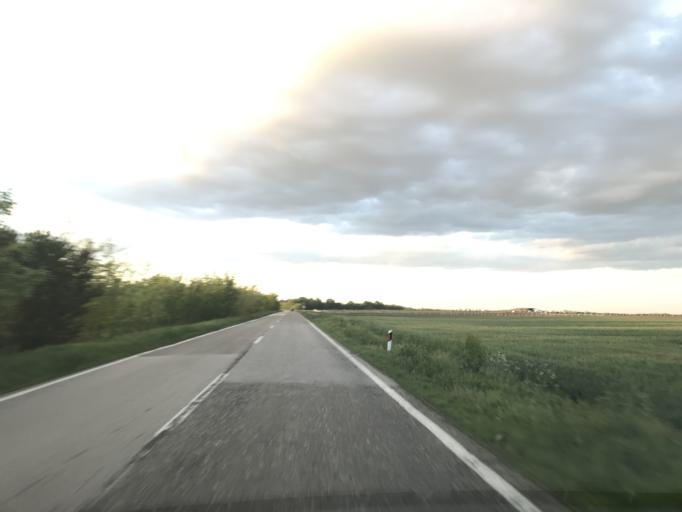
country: RS
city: Banatsko Karadordevo
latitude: 45.6068
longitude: 20.5687
